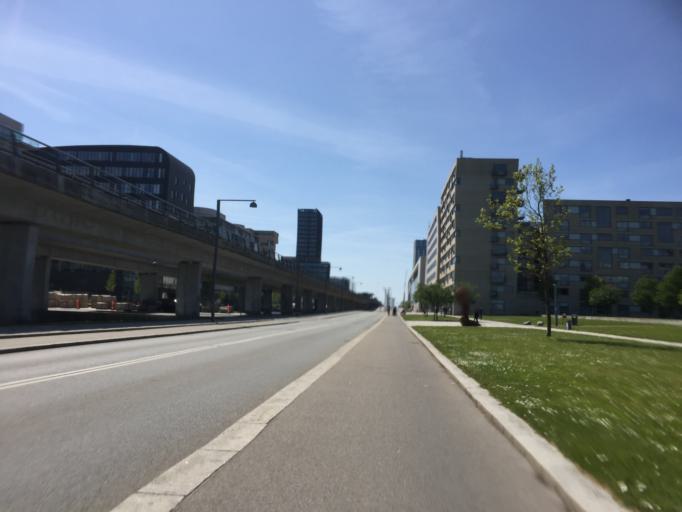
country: DK
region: Capital Region
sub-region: Tarnby Kommune
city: Tarnby
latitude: 55.6336
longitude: 12.5808
